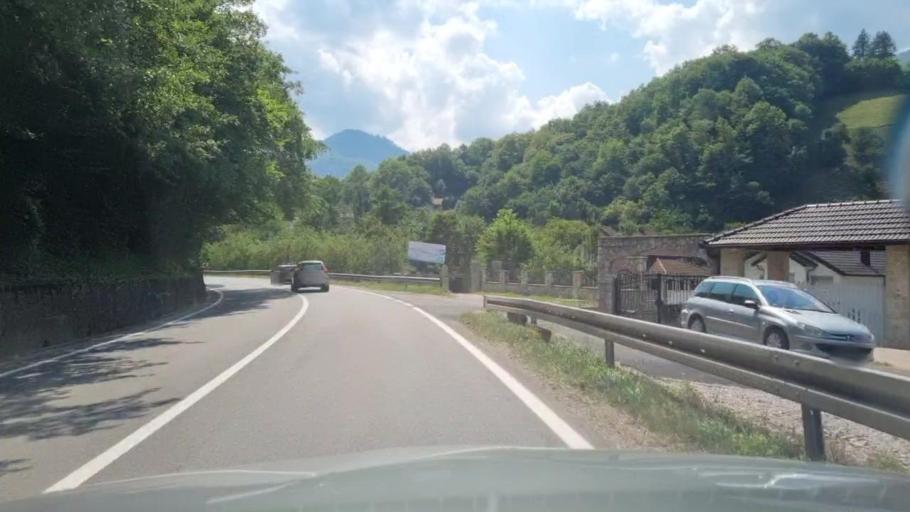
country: BA
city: Stupari
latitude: 44.3276
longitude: 18.6821
